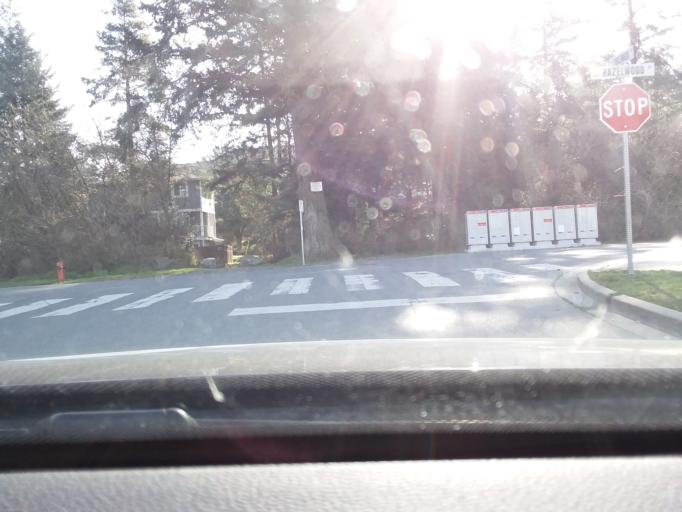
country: CA
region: British Columbia
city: Langford
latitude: 48.4252
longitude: -123.5333
